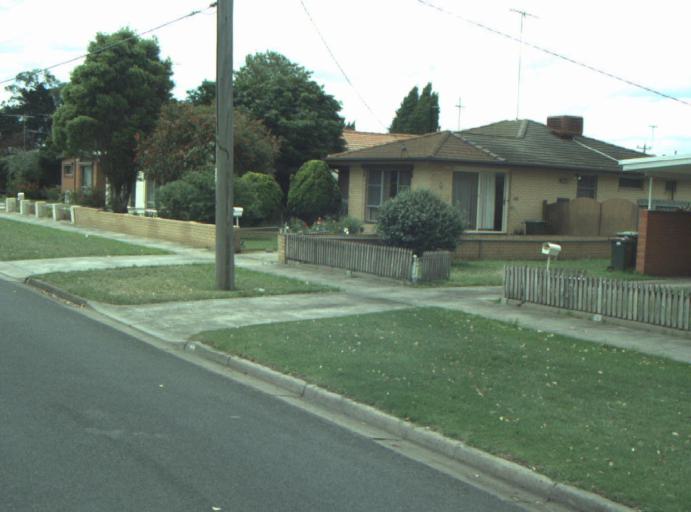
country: AU
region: Victoria
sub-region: Greater Geelong
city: Bell Park
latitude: -38.0746
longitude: 144.3660
